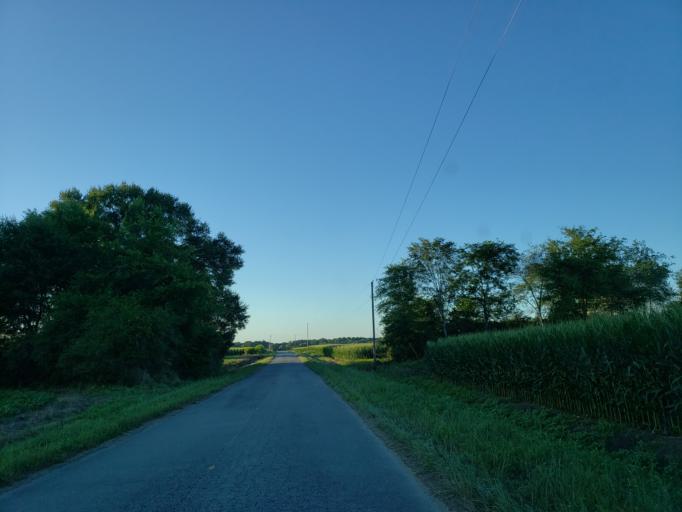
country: US
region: Georgia
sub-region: Bartow County
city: Euharlee
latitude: 34.0848
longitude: -84.9600
